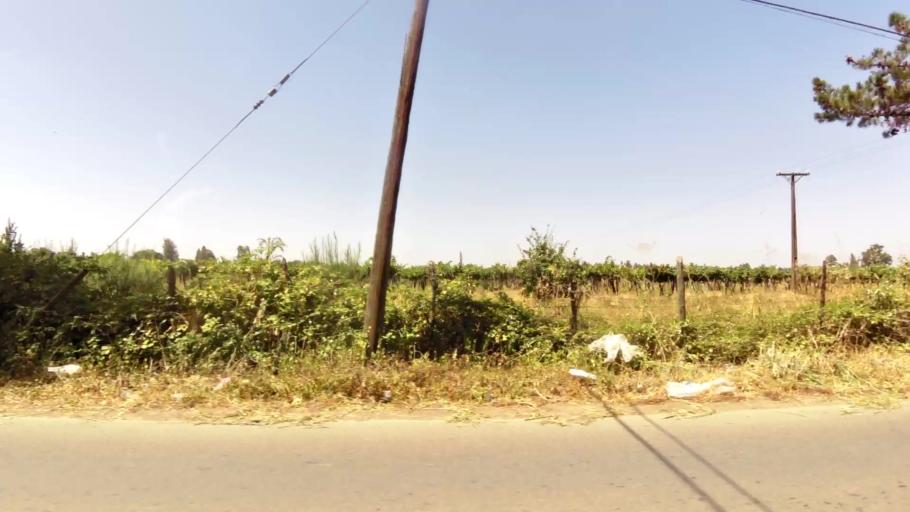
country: CL
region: Maule
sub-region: Provincia de Talca
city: Talca
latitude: -35.4424
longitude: -71.6149
